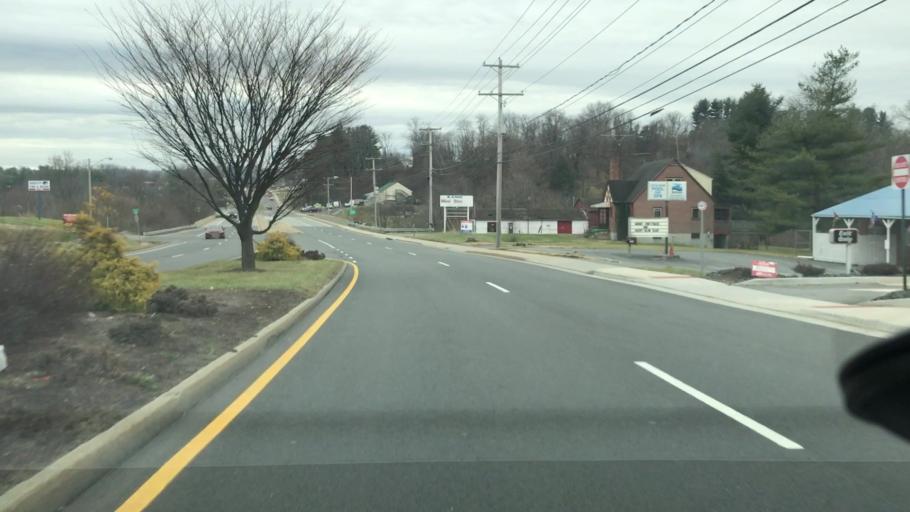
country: US
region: Virginia
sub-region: Montgomery County
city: Christiansburg
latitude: 37.1416
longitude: -80.4152
